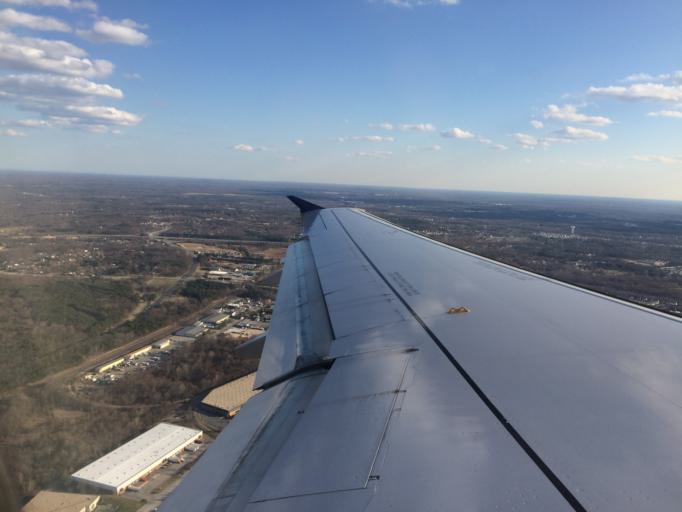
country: US
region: Maryland
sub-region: Howard County
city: Hanover
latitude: 39.1756
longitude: -76.7028
